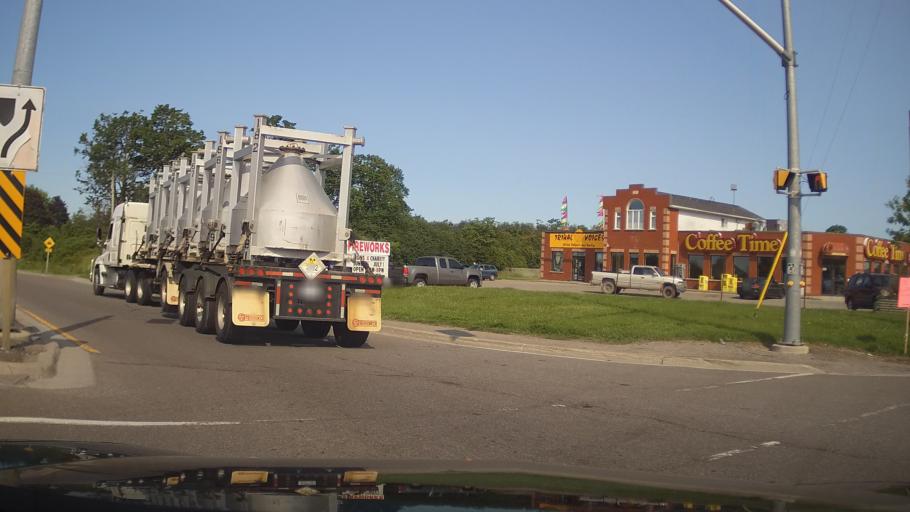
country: CA
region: Ontario
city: Omemee
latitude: 44.3272
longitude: -78.4423
